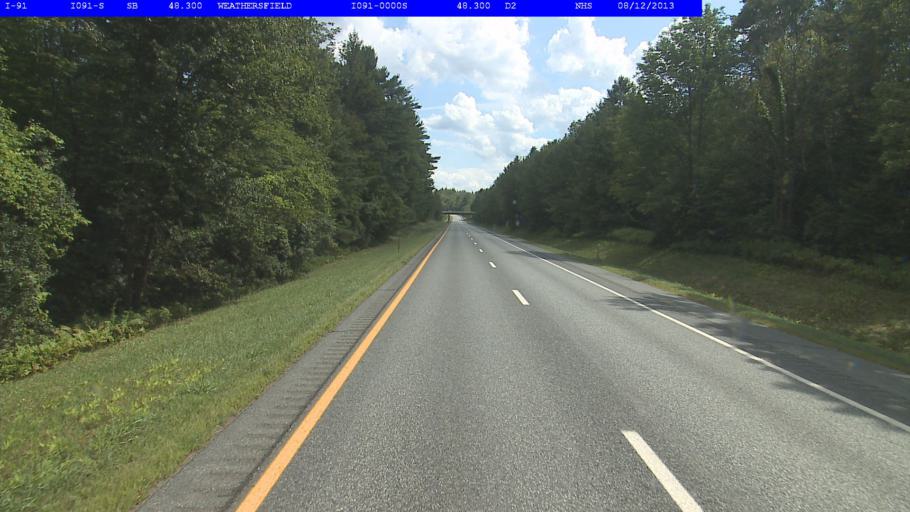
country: US
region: New Hampshire
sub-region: Sullivan County
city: Claremont
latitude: 43.3593
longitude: -72.4241
